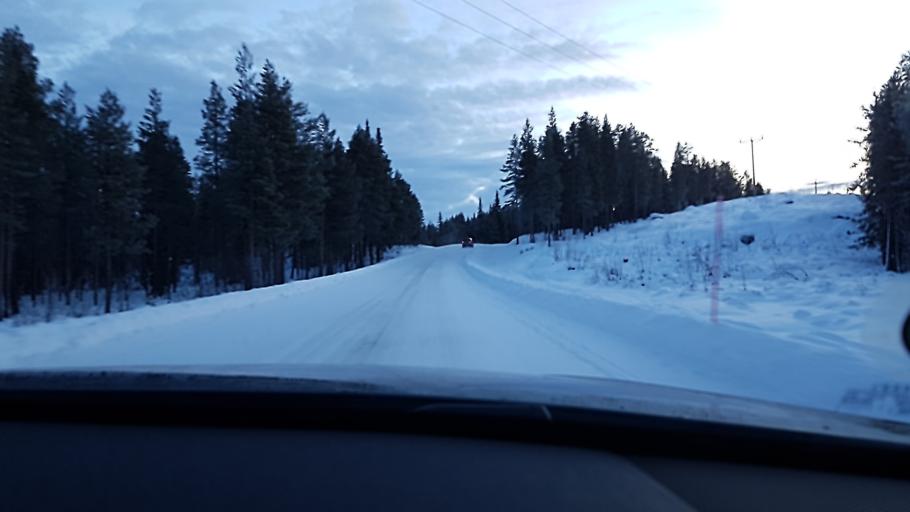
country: SE
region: Vaesterbotten
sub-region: Sorsele Kommun
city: Sorsele
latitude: 65.5009
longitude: 17.5545
